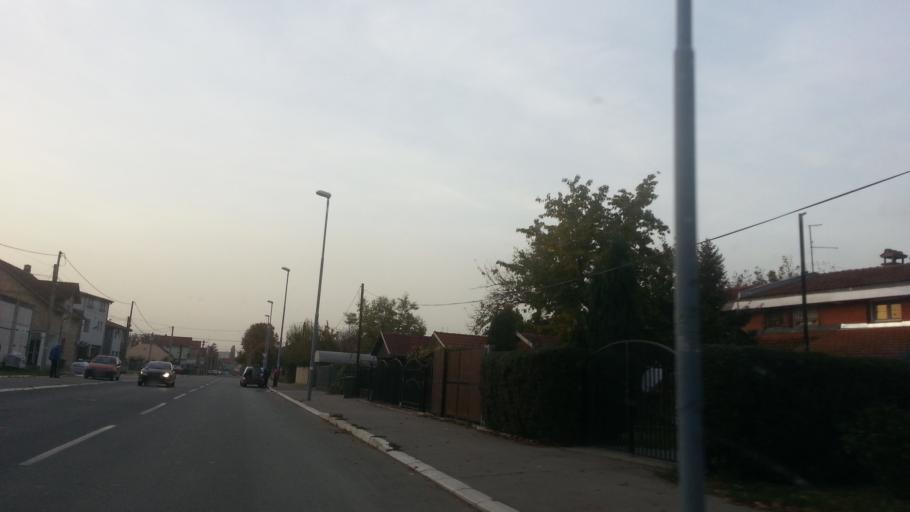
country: RS
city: Novi Banovci
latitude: 44.8926
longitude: 20.2865
